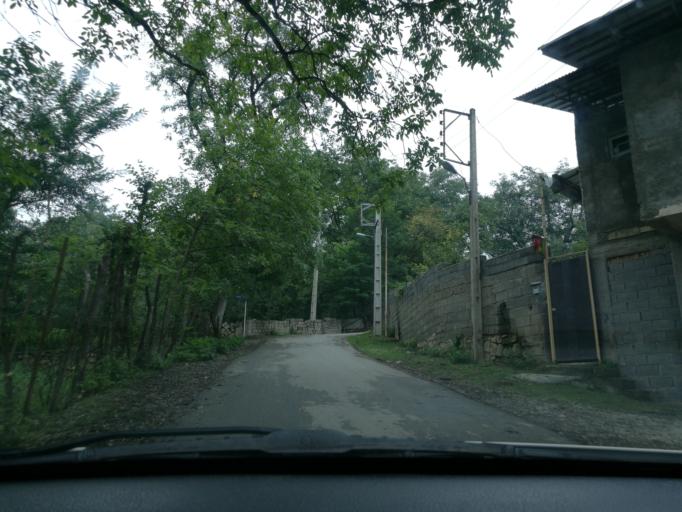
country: IR
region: Mazandaran
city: `Abbasabad
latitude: 36.4949
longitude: 51.2092
